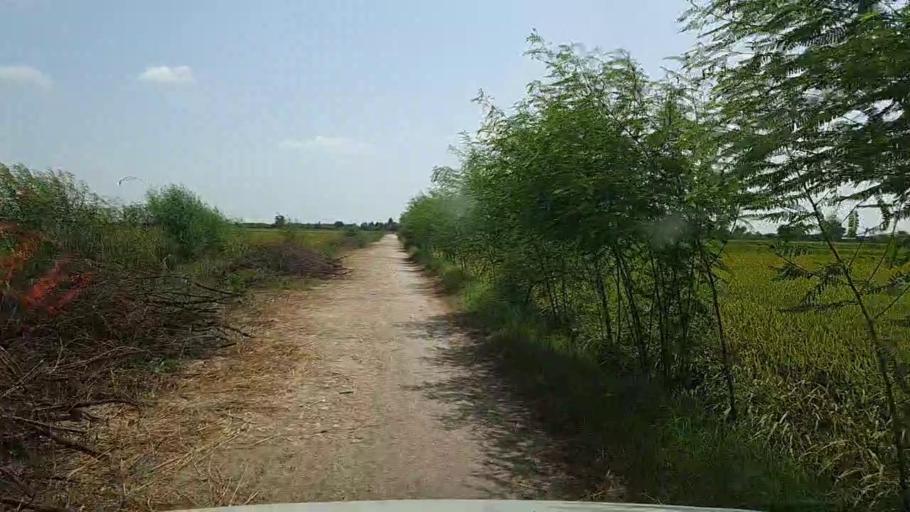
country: PK
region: Sindh
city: Kario
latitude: 24.6366
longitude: 68.5719
